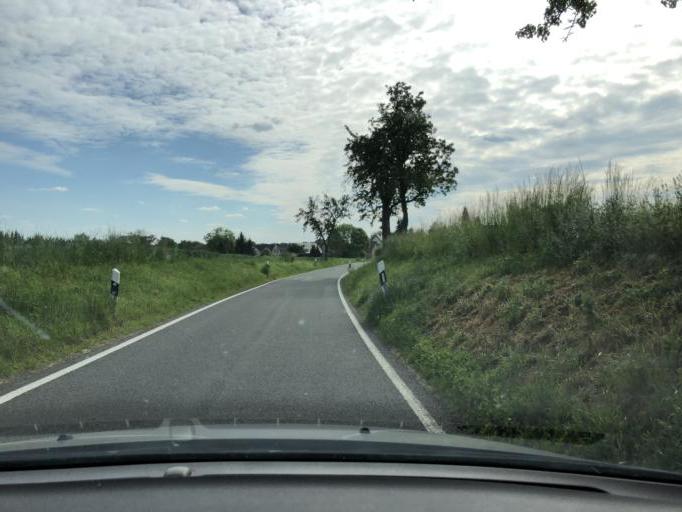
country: DE
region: Saxony
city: Ostrau
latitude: 51.2025
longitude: 12.8255
